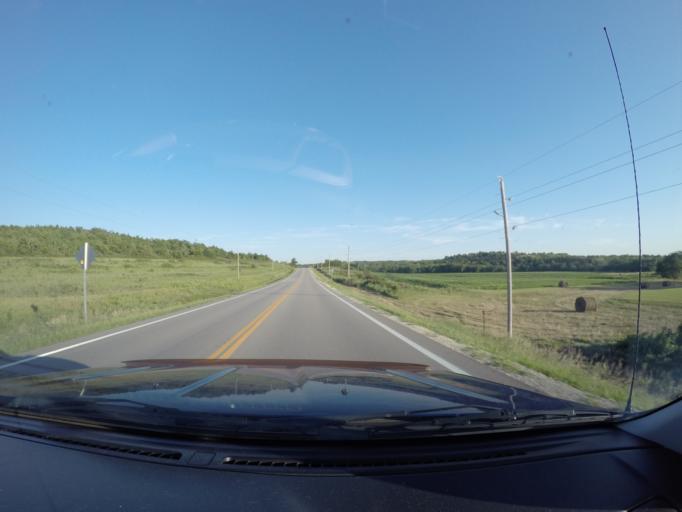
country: US
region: Kansas
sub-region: Pottawatomie County
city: Wamego
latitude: 39.1338
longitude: -96.3013
